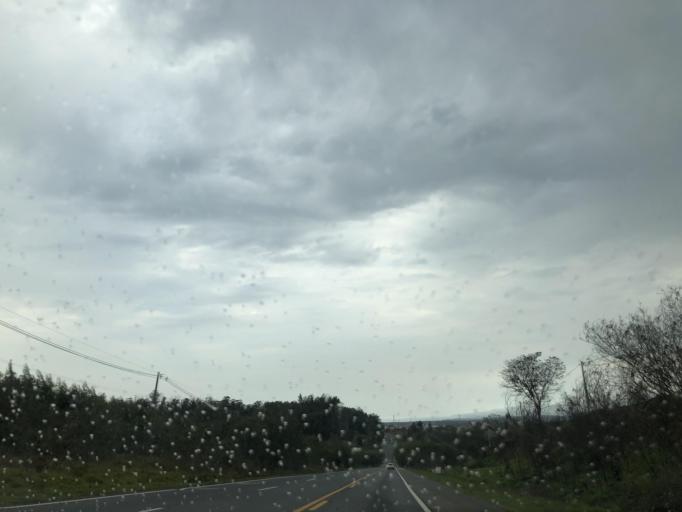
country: BR
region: Sao Paulo
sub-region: Salto De Pirapora
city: Salto de Pirapora
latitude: -23.6632
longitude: -47.5972
